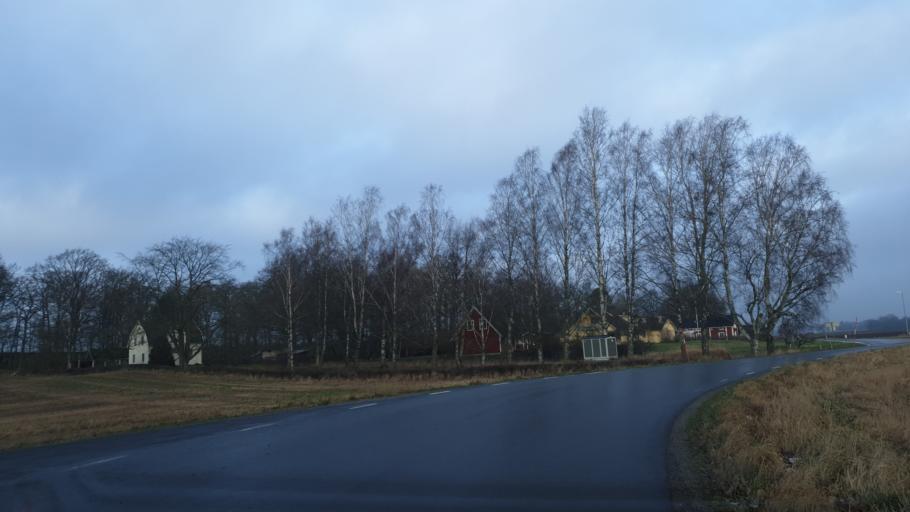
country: SE
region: Blekinge
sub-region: Karlshamns Kommun
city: Morrum
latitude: 56.1645
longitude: 14.7480
